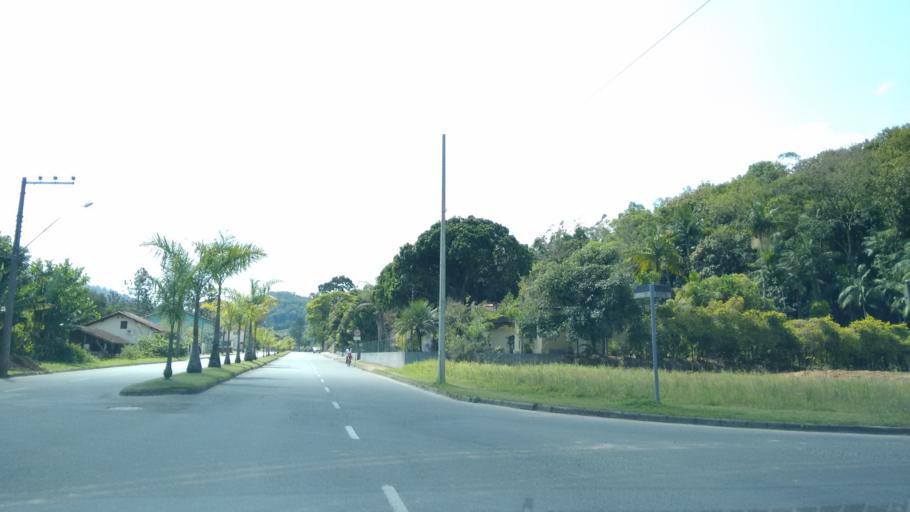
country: BR
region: Santa Catarina
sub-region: Pomerode
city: Pomerode
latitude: -26.7270
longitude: -49.1794
